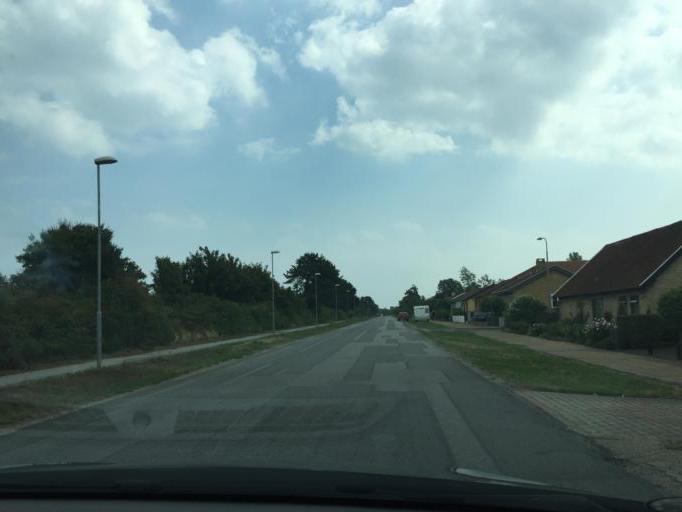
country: DK
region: South Denmark
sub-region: Nyborg Kommune
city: Nyborg
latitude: 55.3082
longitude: 10.8171
